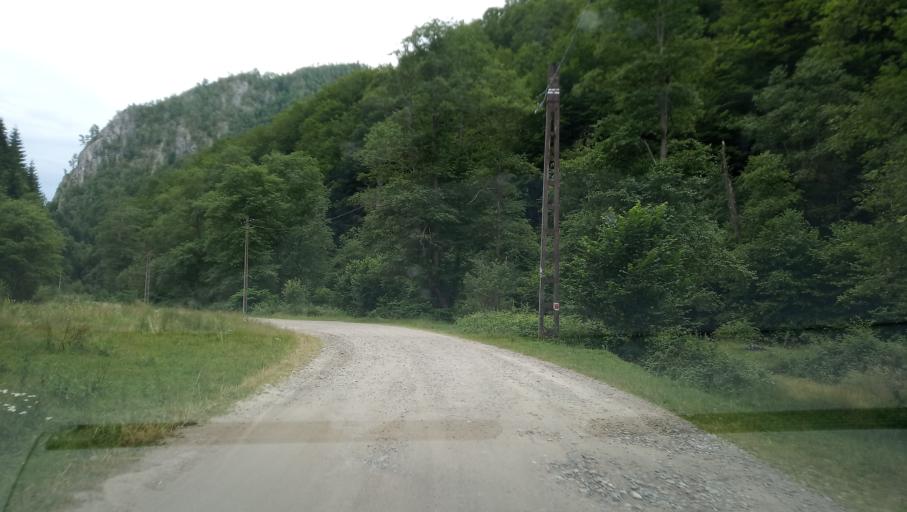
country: RO
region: Hunedoara
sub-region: Oras Petrila
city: Petrila
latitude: 45.4800
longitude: 23.4155
